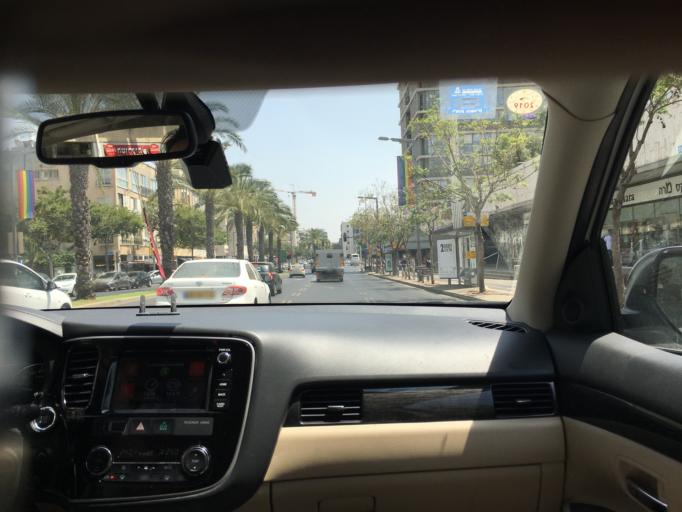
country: IL
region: Tel Aviv
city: Tel Aviv
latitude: 32.0826
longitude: 34.7811
